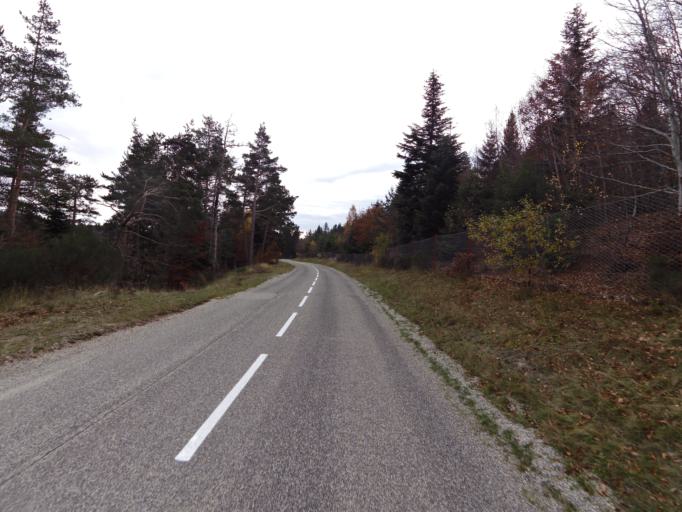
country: FR
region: Rhone-Alpes
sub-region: Departement de l'Ardeche
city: Les Vans
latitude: 44.5640
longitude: 4.0154
